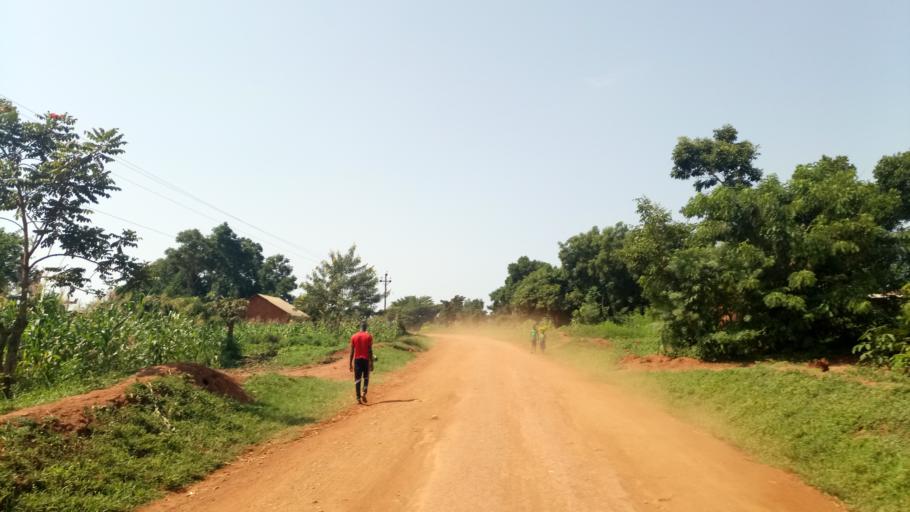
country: UG
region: Eastern Region
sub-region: Kaliro District
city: Kaliro
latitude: 0.9702
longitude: 33.4632
